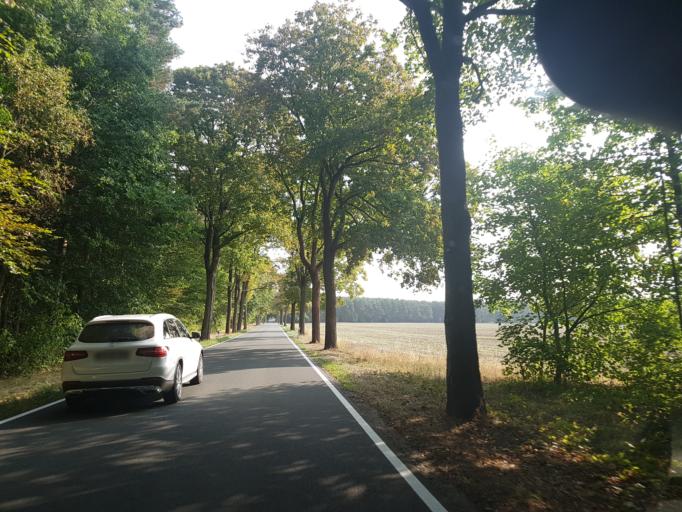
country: DE
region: Brandenburg
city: Wiesenburg
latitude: 52.0722
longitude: 12.3866
